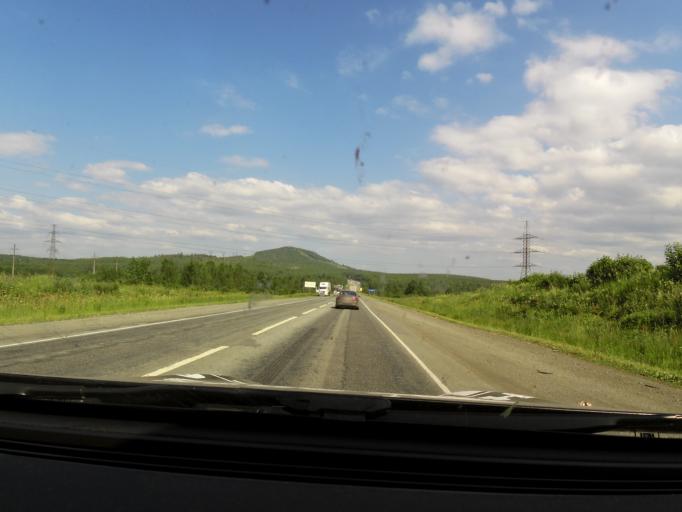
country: RU
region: Sverdlovsk
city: Revda
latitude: 56.8271
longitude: 59.9590
